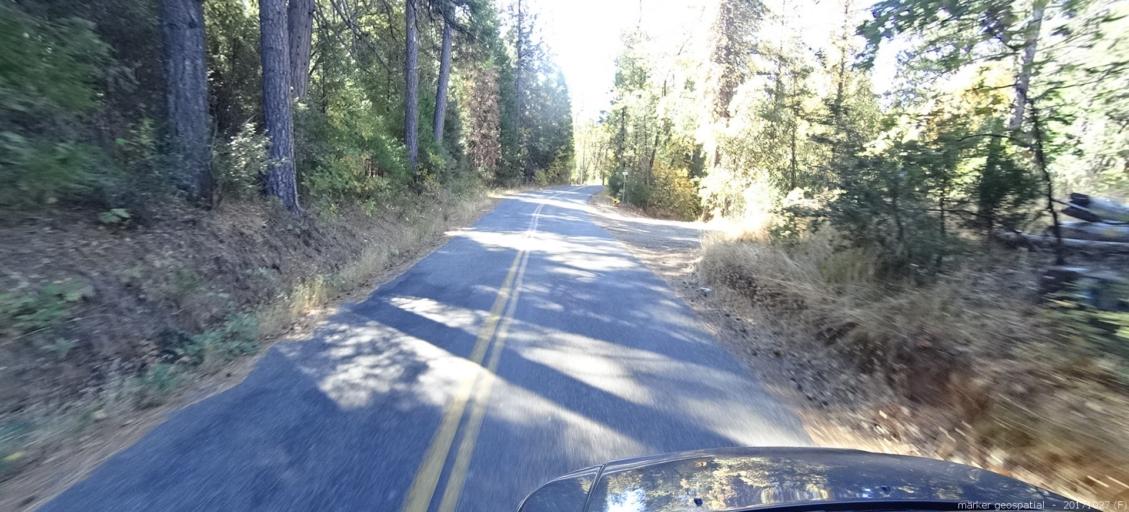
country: US
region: California
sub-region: Shasta County
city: Shingletown
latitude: 40.7421
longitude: -121.9513
